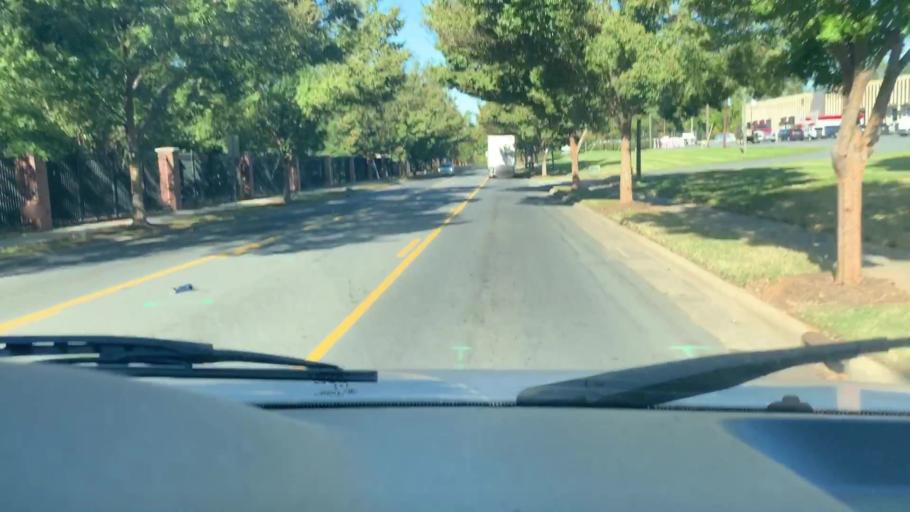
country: US
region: North Carolina
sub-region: Mecklenburg County
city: Charlotte
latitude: 35.2621
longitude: -80.8279
